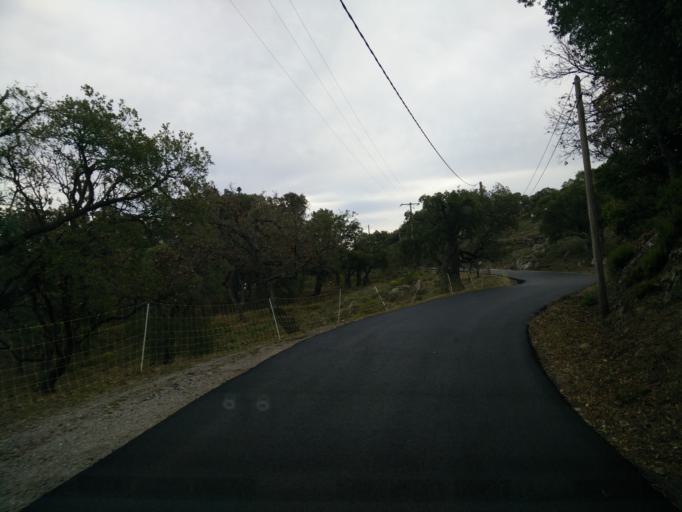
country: FR
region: Provence-Alpes-Cote d'Azur
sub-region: Departement du Var
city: Sainte-Maxime
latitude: 43.3672
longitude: 6.6166
